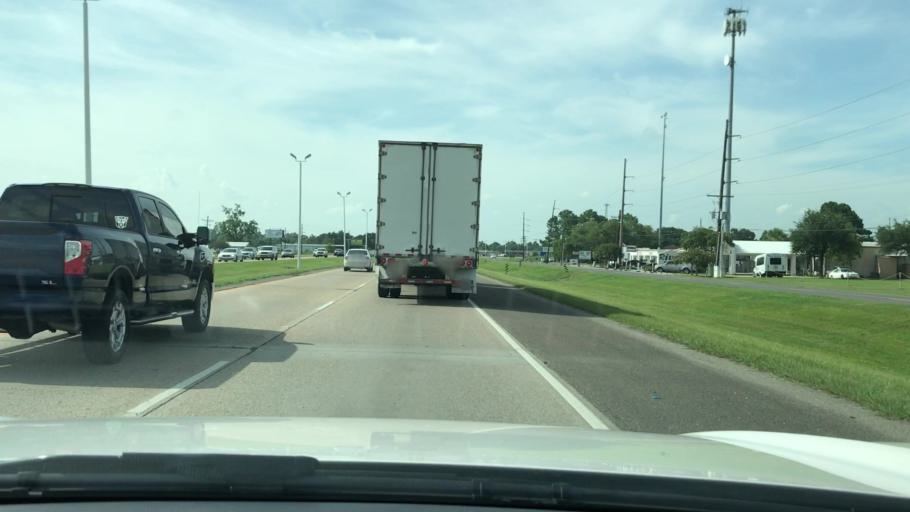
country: US
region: Louisiana
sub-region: West Baton Rouge Parish
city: Addis
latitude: 30.3580
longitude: -91.2600
